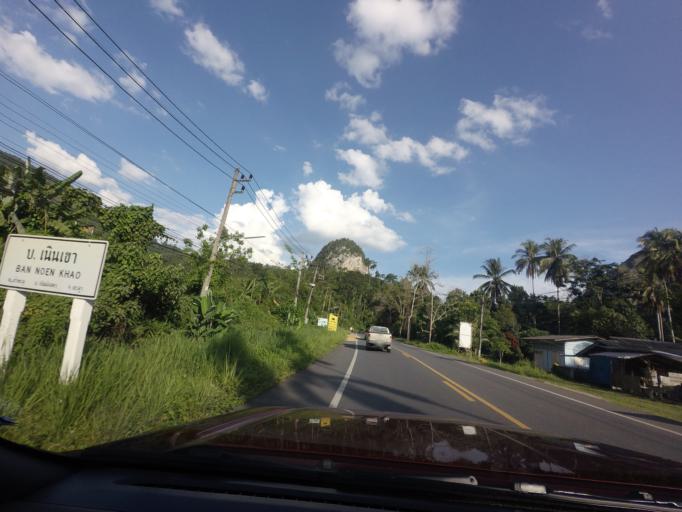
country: TH
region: Yala
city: Than To
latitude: 6.2176
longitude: 101.1657
